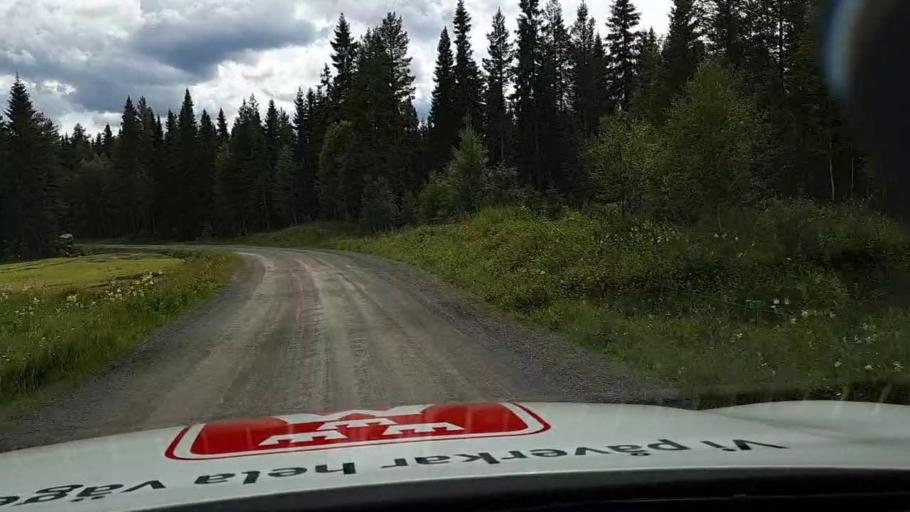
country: SE
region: Jaemtland
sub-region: Braecke Kommun
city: Braecke
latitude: 63.2791
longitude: 15.3708
